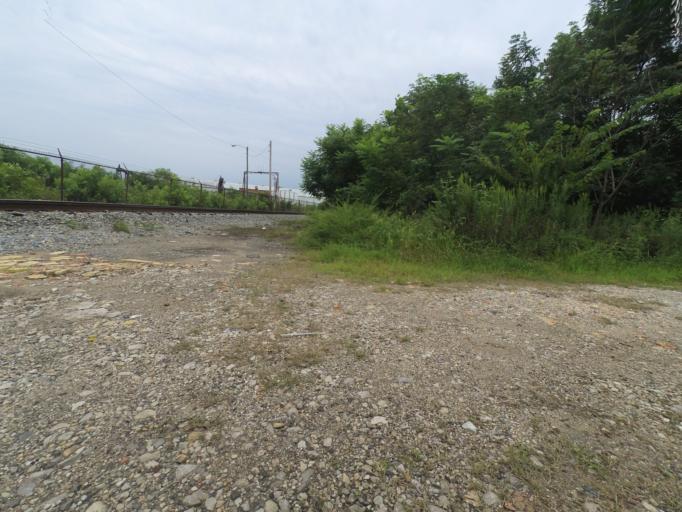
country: US
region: West Virginia
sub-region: Cabell County
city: Huntington
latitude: 38.4294
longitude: -82.4207
